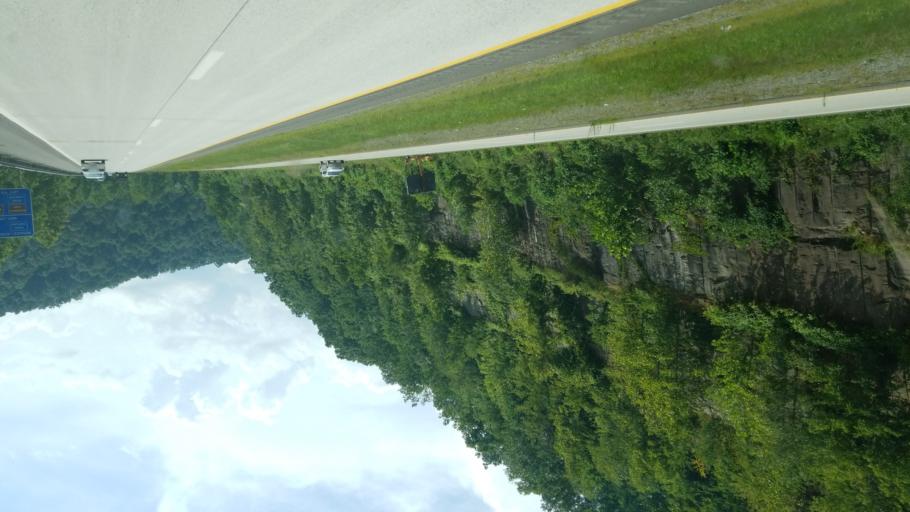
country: US
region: West Virginia
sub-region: Kanawha County
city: Alum Creek
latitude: 38.1893
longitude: -81.8480
